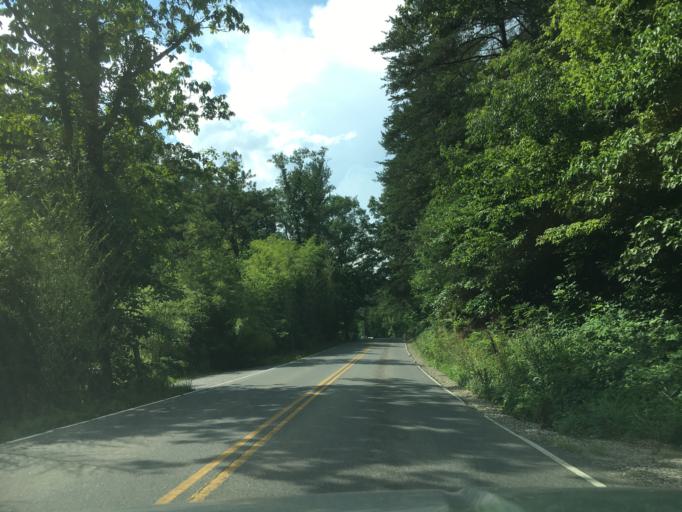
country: US
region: Virginia
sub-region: Roanoke County
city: Cave Spring
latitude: 37.2044
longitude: -80.0075
